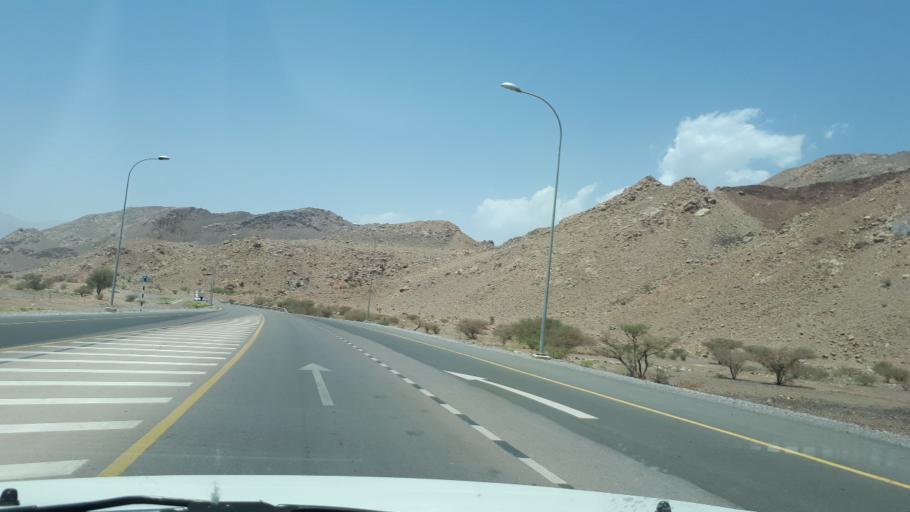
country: OM
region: Muhafazat ad Dakhiliyah
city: Bahla'
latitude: 23.0492
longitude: 57.3105
